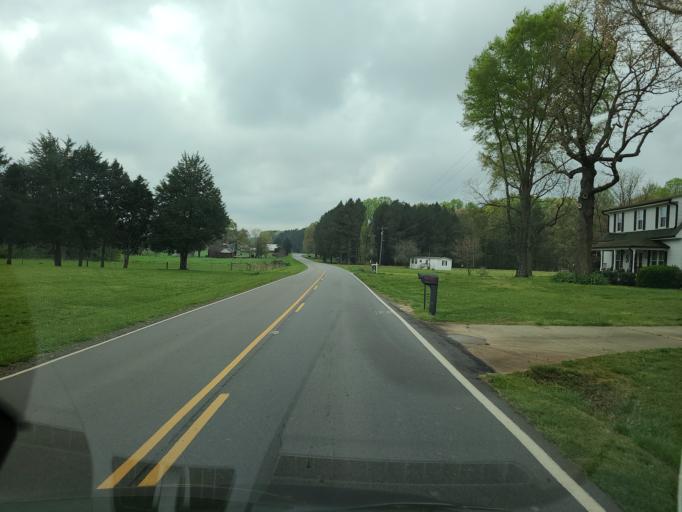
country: US
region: North Carolina
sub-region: Lincoln County
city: Lincolnton
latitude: 35.4609
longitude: -81.2988
